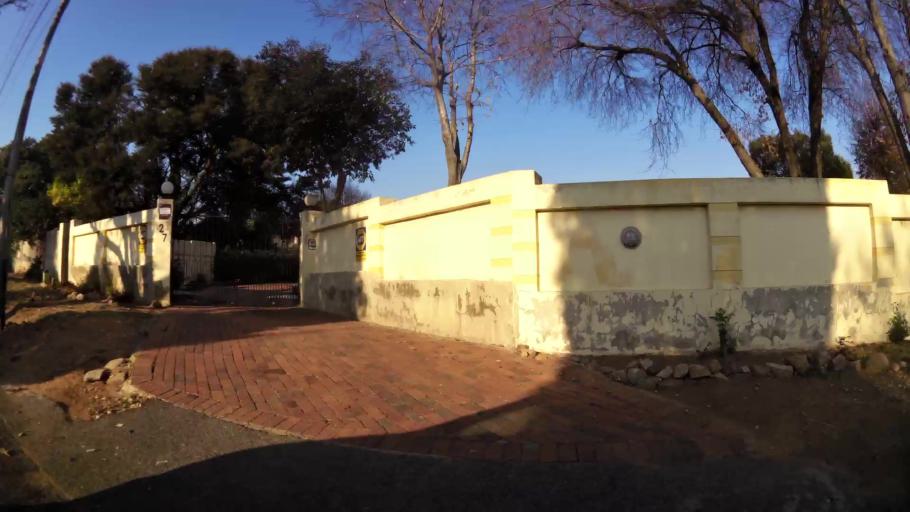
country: ZA
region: Gauteng
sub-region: City of Johannesburg Metropolitan Municipality
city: Modderfontein
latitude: -26.0802
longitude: 28.0932
